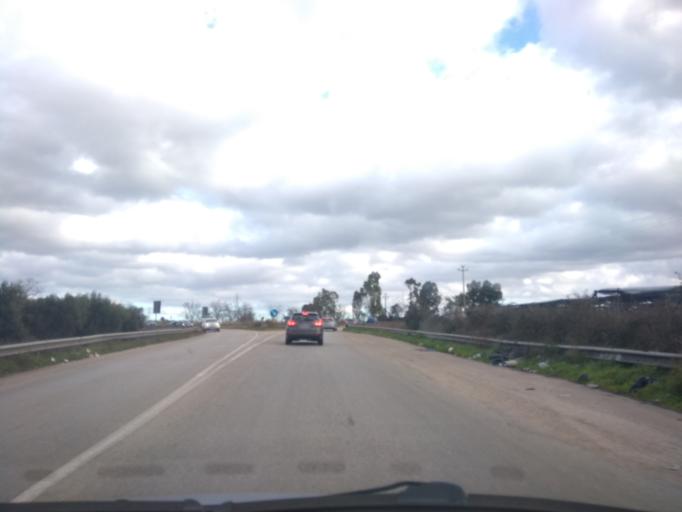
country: IT
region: Apulia
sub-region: Provincia di Bari
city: Cellamare
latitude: 41.0026
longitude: 16.9103
